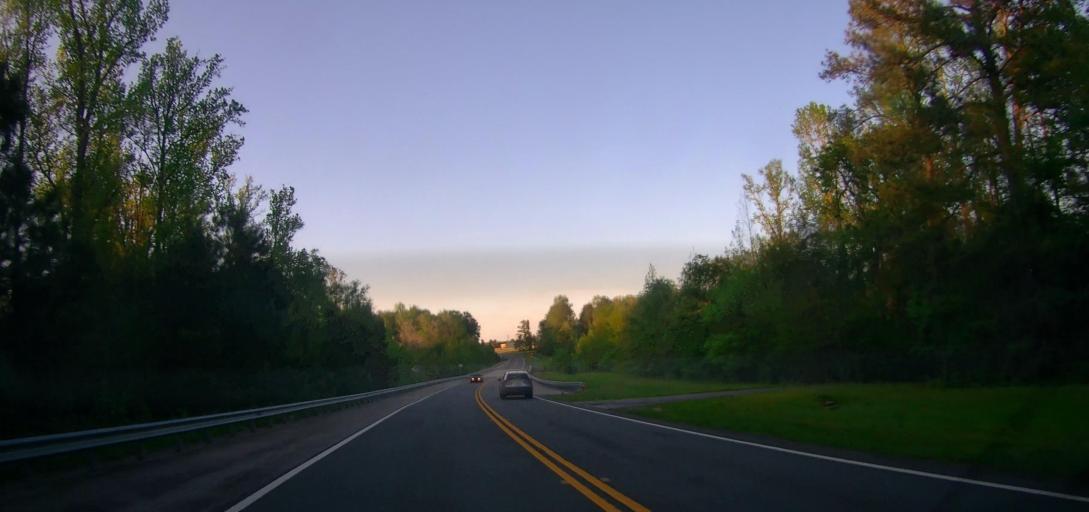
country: US
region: Georgia
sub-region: Talbot County
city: Talbotton
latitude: 32.5324
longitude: -84.6052
